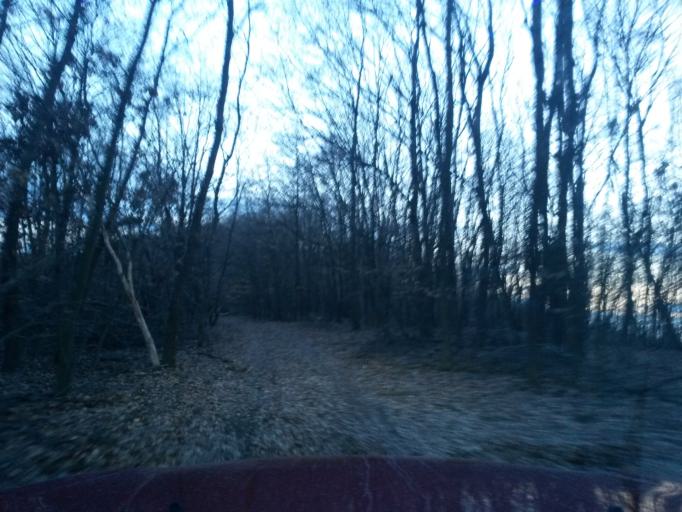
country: SK
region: Kosicky
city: Kosice
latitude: 48.6985
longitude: 21.3820
